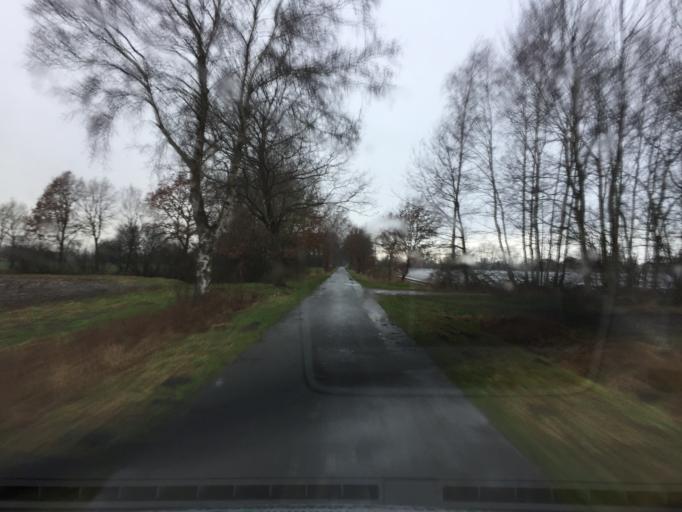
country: DE
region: Lower Saxony
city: Hassel
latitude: 52.6585
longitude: 8.8411
